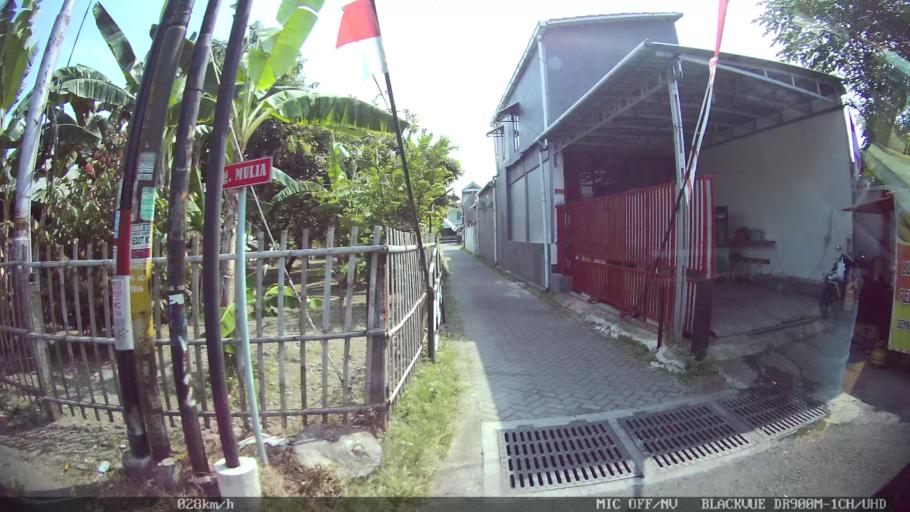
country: ID
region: Daerah Istimewa Yogyakarta
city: Yogyakarta
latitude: -7.8119
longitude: 110.3885
